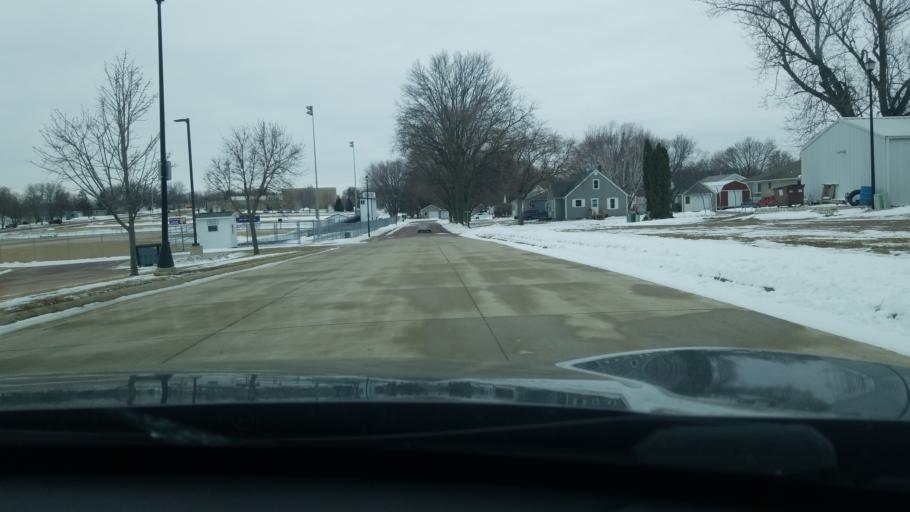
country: US
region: Iowa
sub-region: Lyon County
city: Rock Rapids
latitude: 43.4248
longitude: -96.1701
